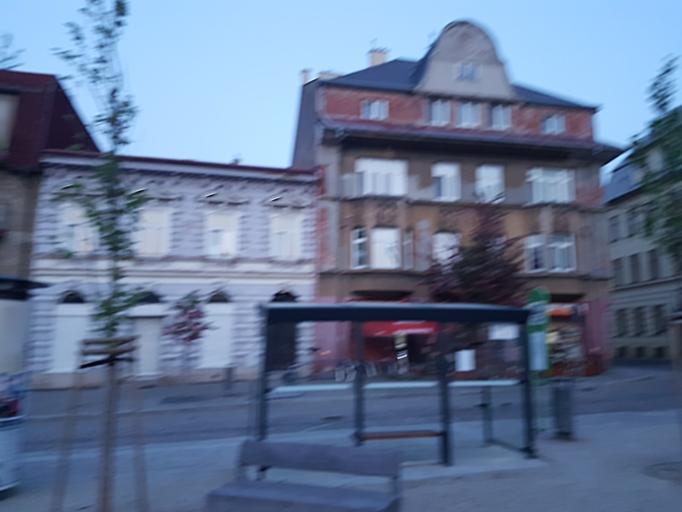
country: CZ
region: Moravskoslezsky
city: Stary Bohumin
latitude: 49.9194
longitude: 18.3289
